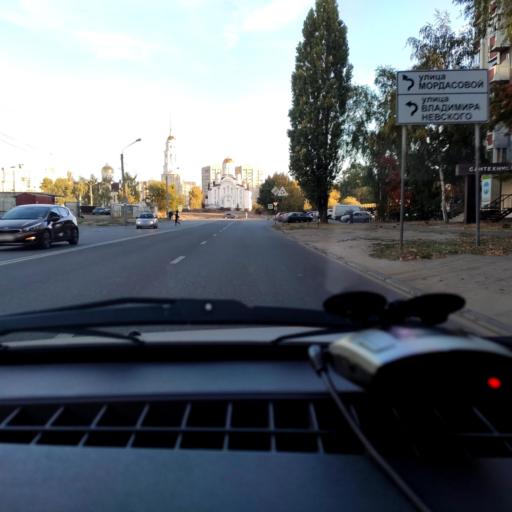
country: RU
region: Voronezj
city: Podgornoye
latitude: 51.7141
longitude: 39.1734
